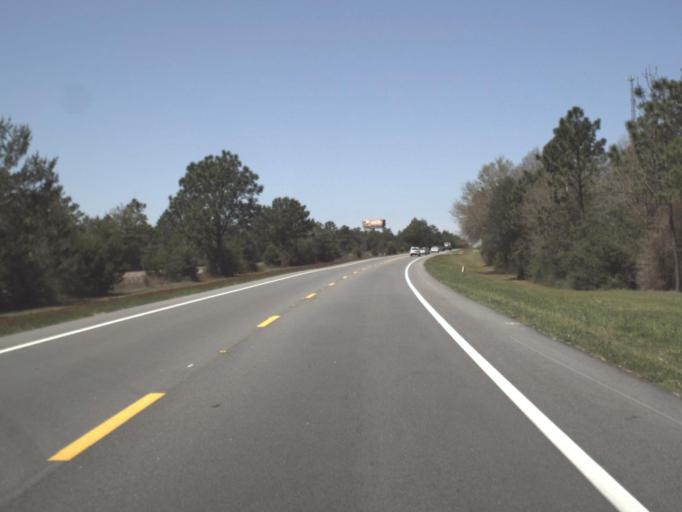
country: US
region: Florida
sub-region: Walton County
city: DeFuniak Springs
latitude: 30.7467
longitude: -86.2313
